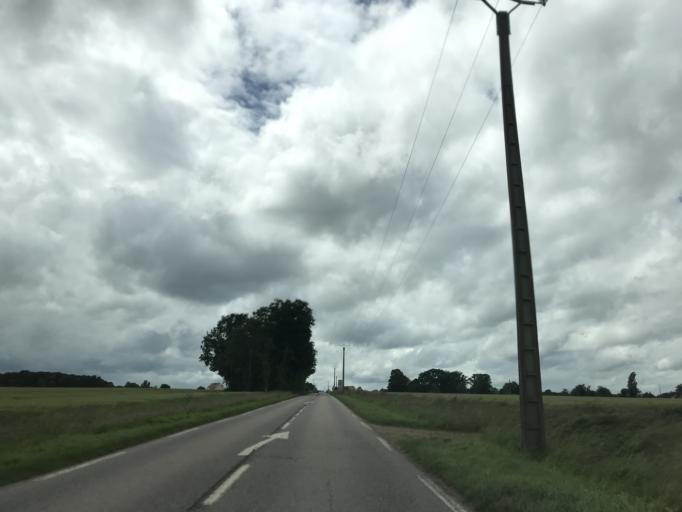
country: FR
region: Ile-de-France
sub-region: Departement des Yvelines
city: Breval
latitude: 48.9582
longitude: 1.5168
